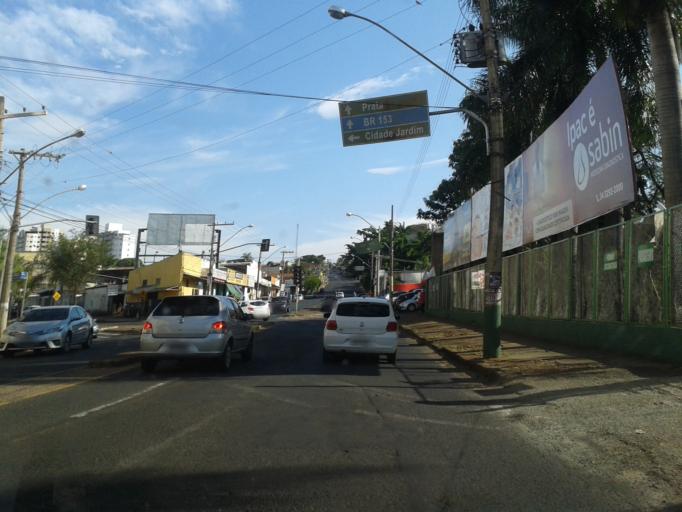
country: BR
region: Minas Gerais
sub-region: Uberlandia
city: Uberlandia
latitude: -18.9304
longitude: -48.2942
